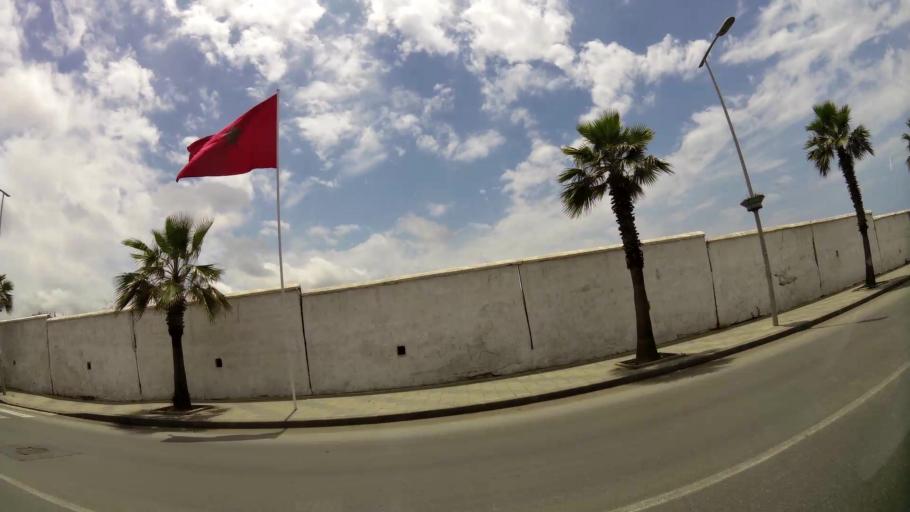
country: MA
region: Rabat-Sale-Zemmour-Zaer
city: Sale
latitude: 34.0353
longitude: -6.8123
